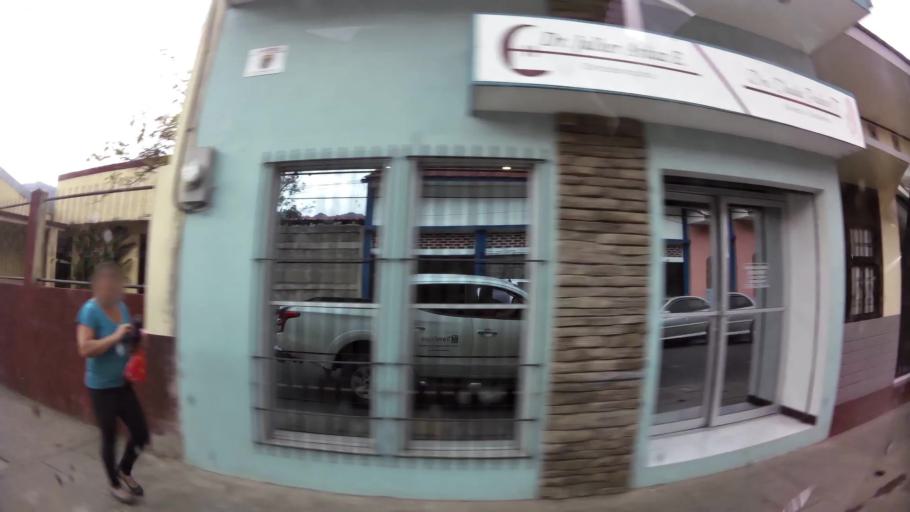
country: NI
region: Jinotega
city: Jinotega
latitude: 13.0937
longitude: -86.0037
